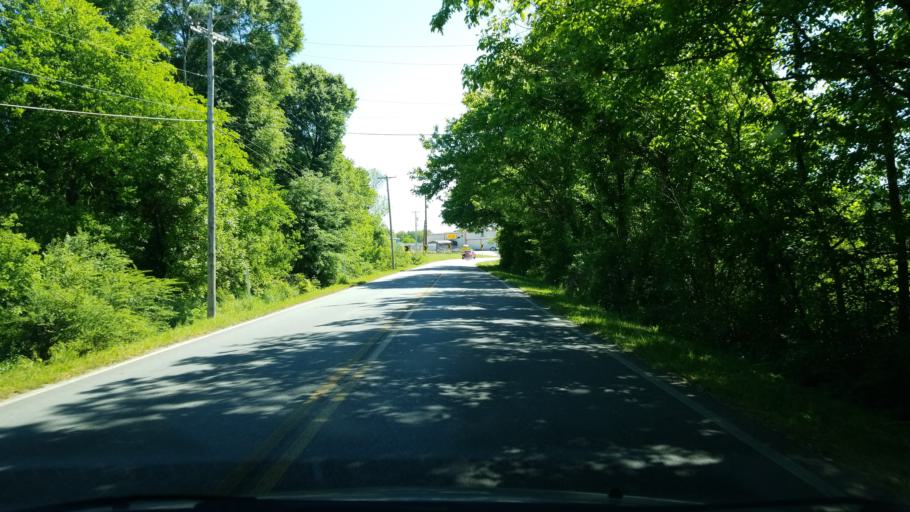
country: US
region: Tennessee
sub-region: Hamilton County
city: Middle Valley
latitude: 35.1732
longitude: -85.2100
